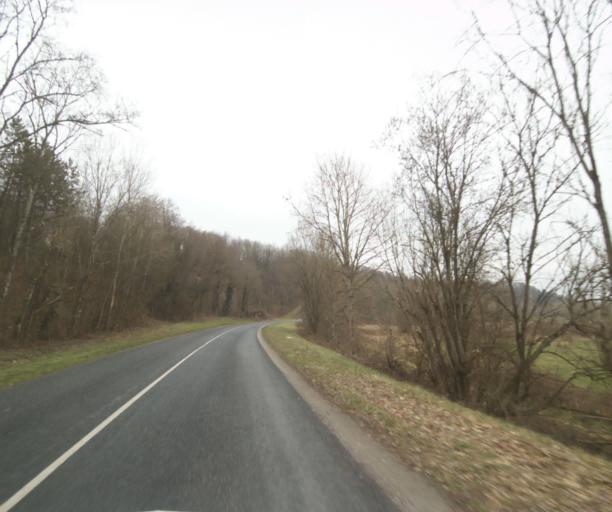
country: FR
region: Champagne-Ardenne
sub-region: Departement de la Haute-Marne
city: Bienville
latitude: 48.5694
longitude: 5.0387
